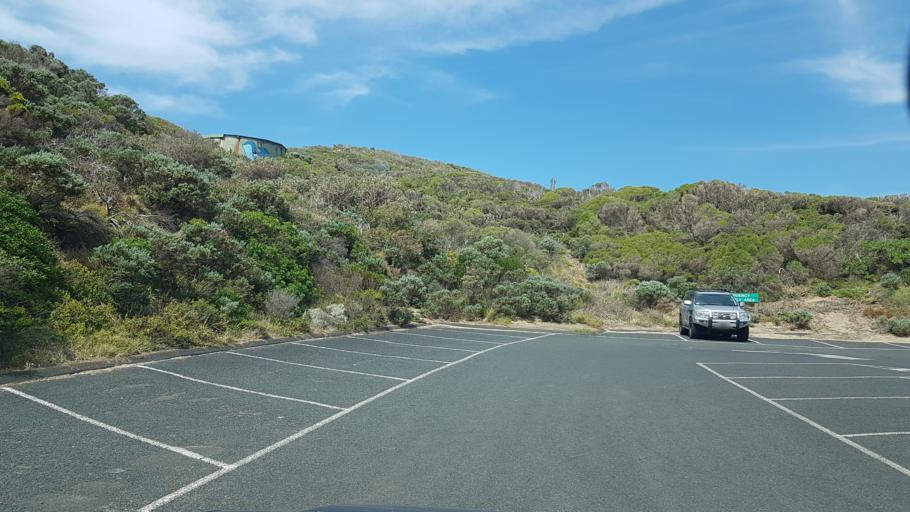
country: AU
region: Victoria
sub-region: Mornington Peninsula
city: Sorrento
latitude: -38.3345
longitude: 144.7055
